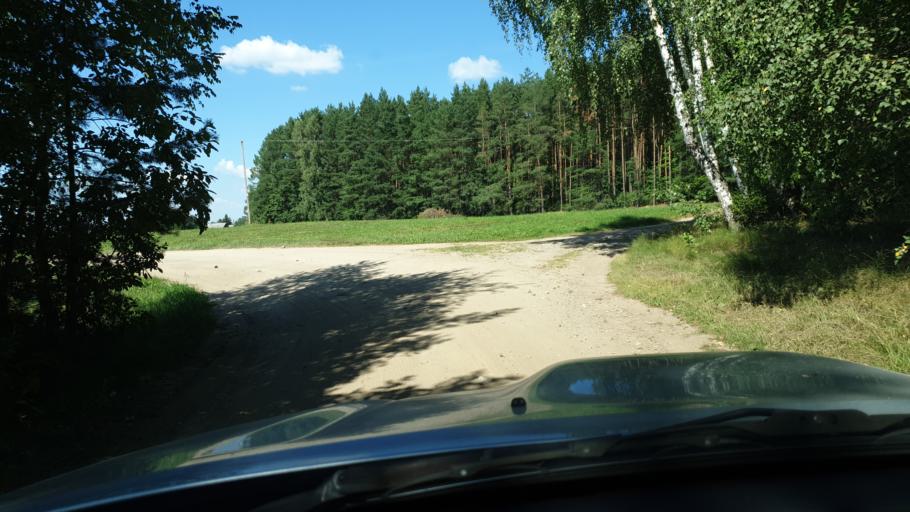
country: LT
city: Sirvintos
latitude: 54.9145
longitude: 24.9250
